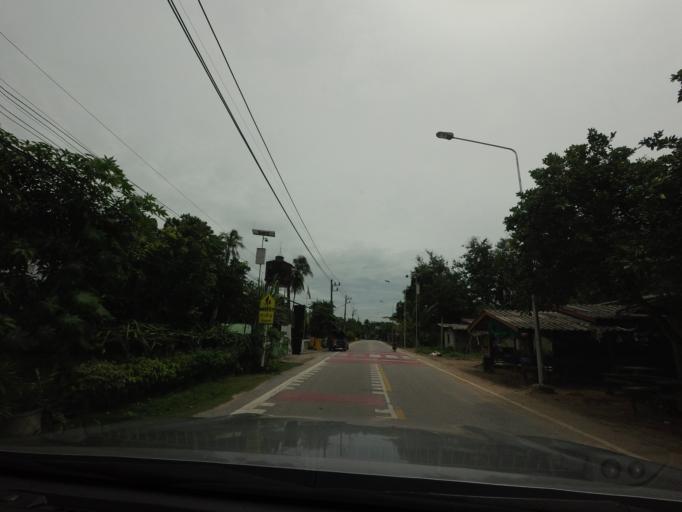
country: TH
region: Pattani
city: Kapho
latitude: 6.5789
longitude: 101.5353
